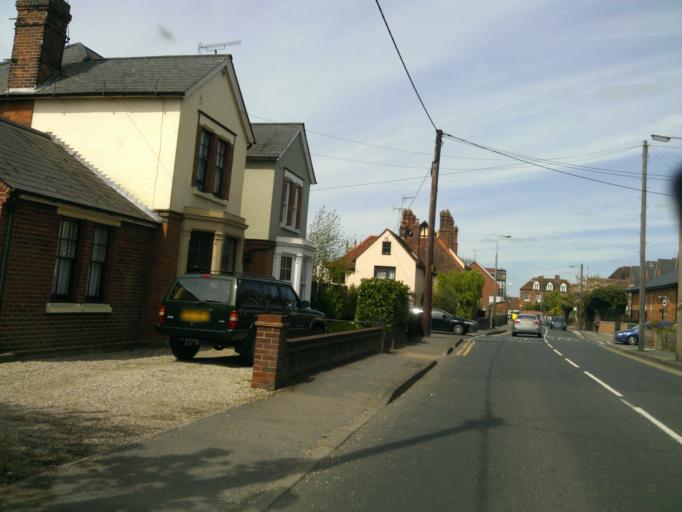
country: GB
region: England
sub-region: Essex
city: Earls Colne
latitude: 51.9444
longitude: 0.6432
